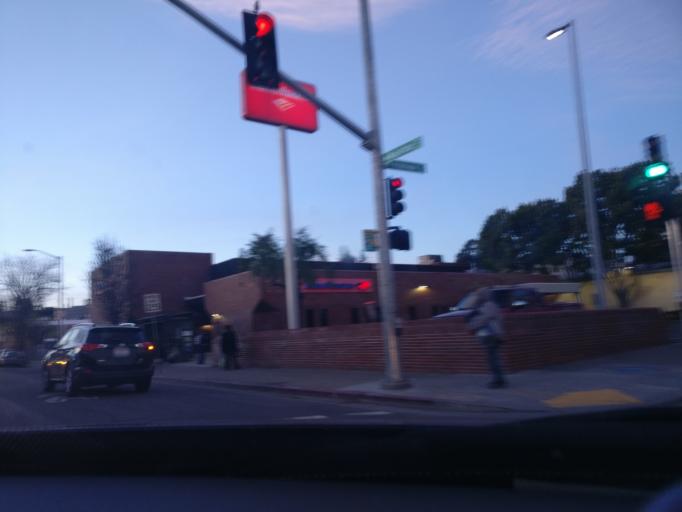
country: US
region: California
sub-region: Alameda County
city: Piedmont
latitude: 37.8004
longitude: -122.2162
